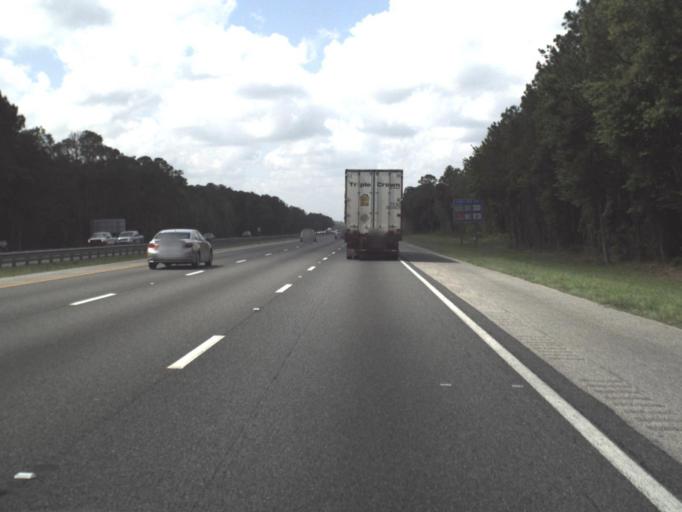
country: US
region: Florida
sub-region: Saint Johns County
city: Fruit Cove
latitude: 30.0487
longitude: -81.4969
